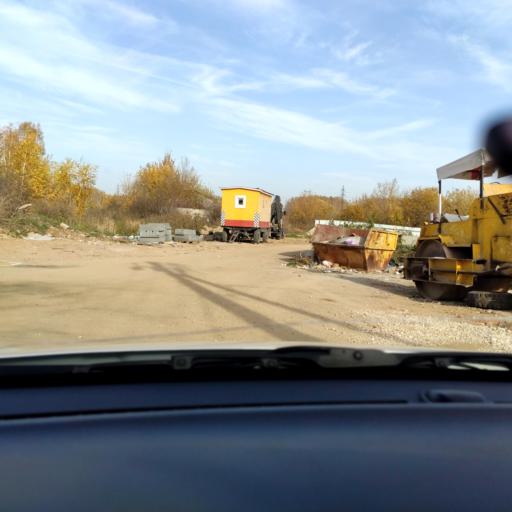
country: RU
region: Tatarstan
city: Vysokaya Gora
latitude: 55.8083
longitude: 49.2725
